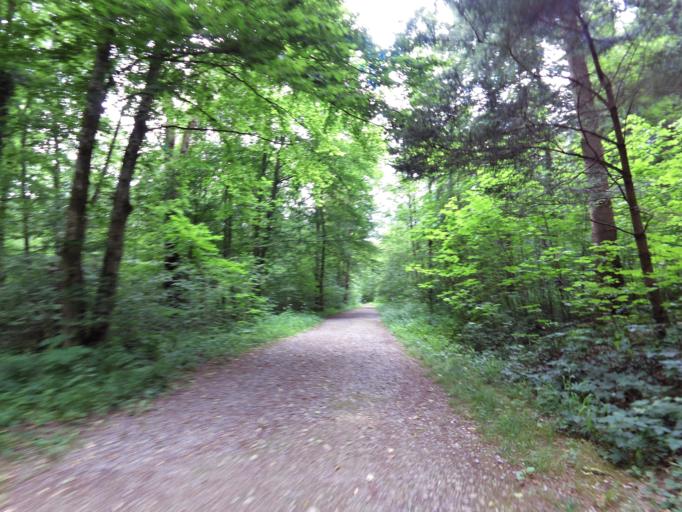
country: CH
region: Zurich
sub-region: Bezirk Zuerich
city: Zuerich (Kreis 10)
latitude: 47.4109
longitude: 8.5008
